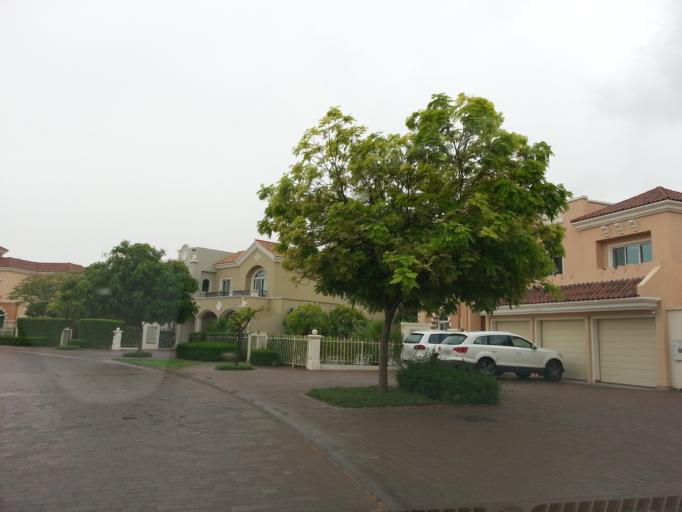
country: AE
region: Dubai
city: Dubai
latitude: 25.0328
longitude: 55.2137
